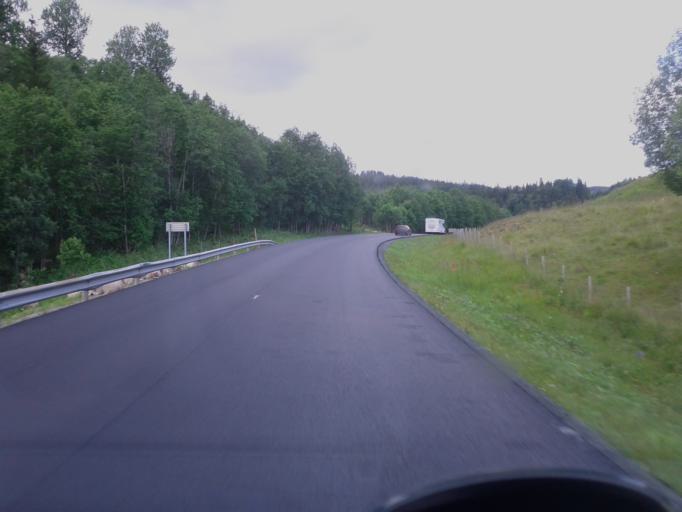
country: NO
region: Nord-Trondelag
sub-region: Grong
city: Grong
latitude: 64.5294
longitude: 12.3983
